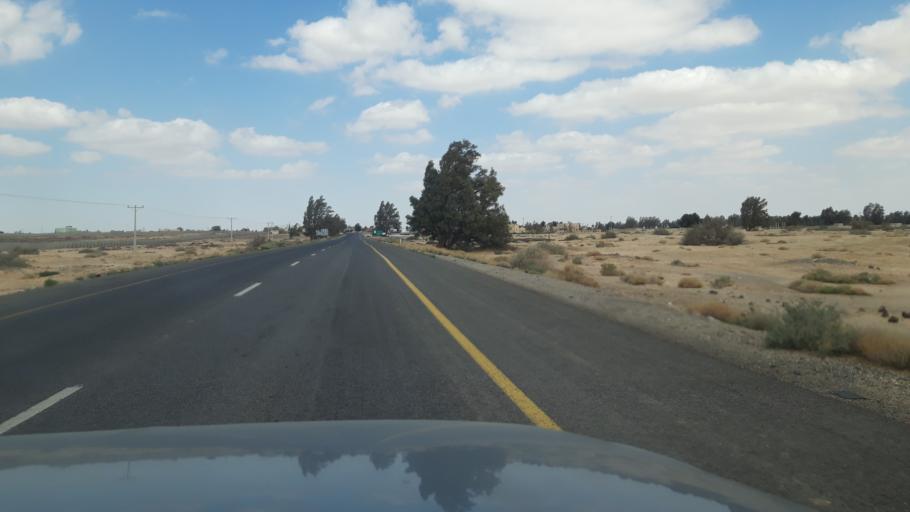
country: JO
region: Amman
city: Al Azraq ash Shamali
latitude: 31.8212
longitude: 36.8090
